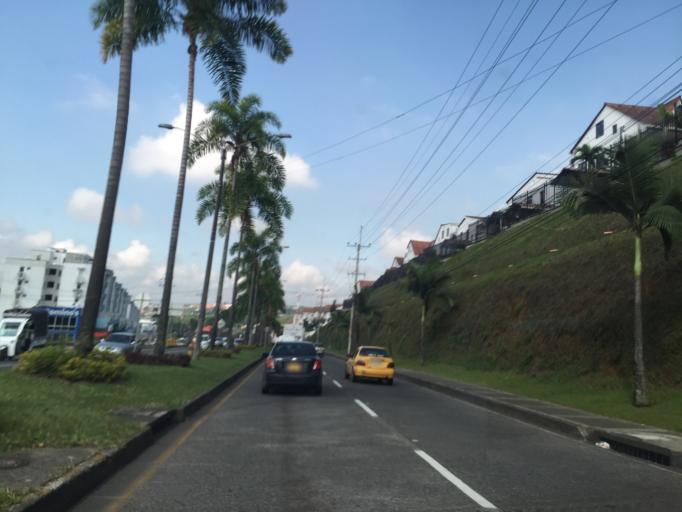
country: CO
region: Risaralda
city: Pereira
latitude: 4.8070
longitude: -75.7196
